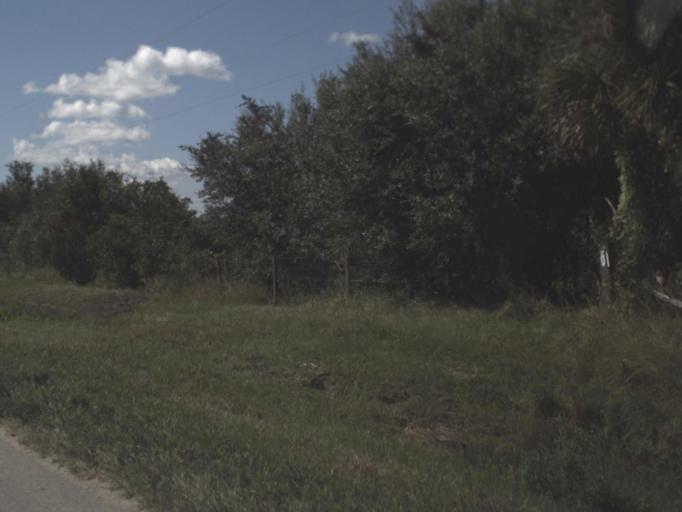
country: US
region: Florida
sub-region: Hendry County
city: Port LaBelle
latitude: 26.8130
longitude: -81.3170
